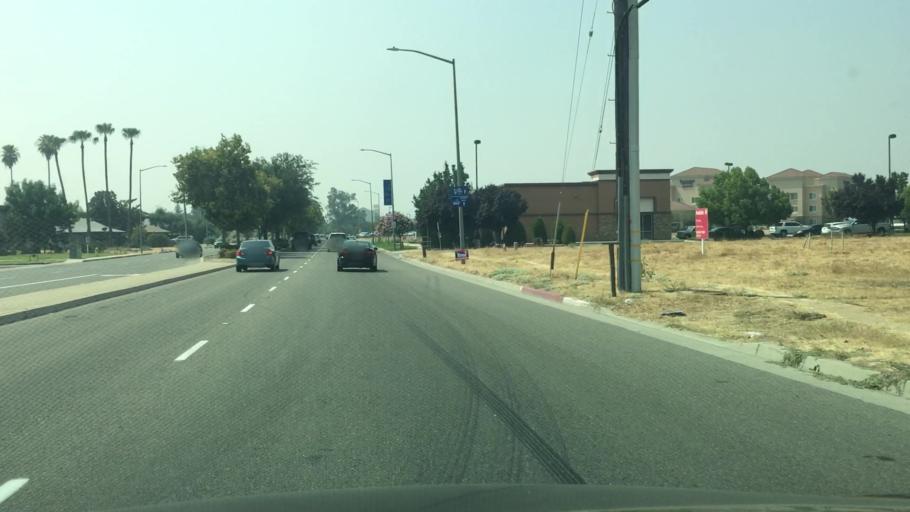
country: US
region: California
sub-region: Fresno County
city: Clovis
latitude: 36.8337
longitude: -119.7002
